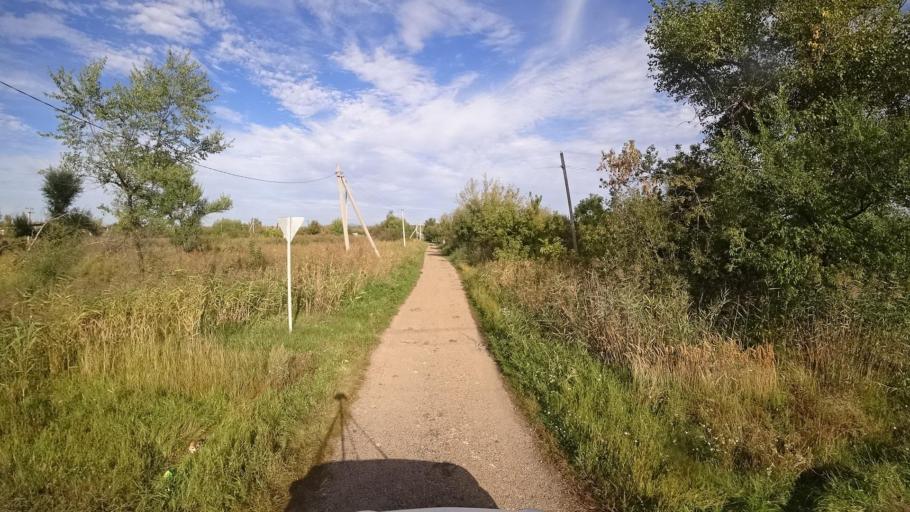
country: RU
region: Primorskiy
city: Dostoyevka
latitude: 44.2910
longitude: 133.4266
